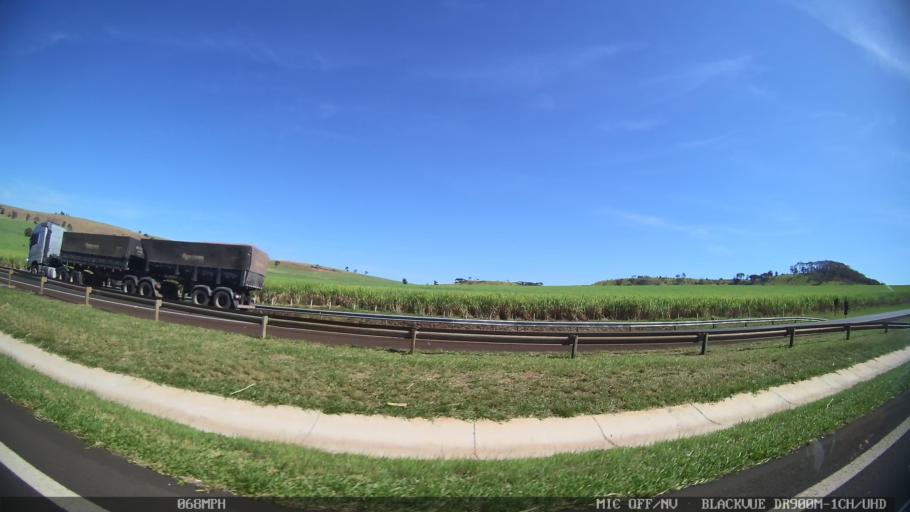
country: BR
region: Sao Paulo
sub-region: Sao Simao
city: Sao Simao
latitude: -21.4339
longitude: -47.6522
